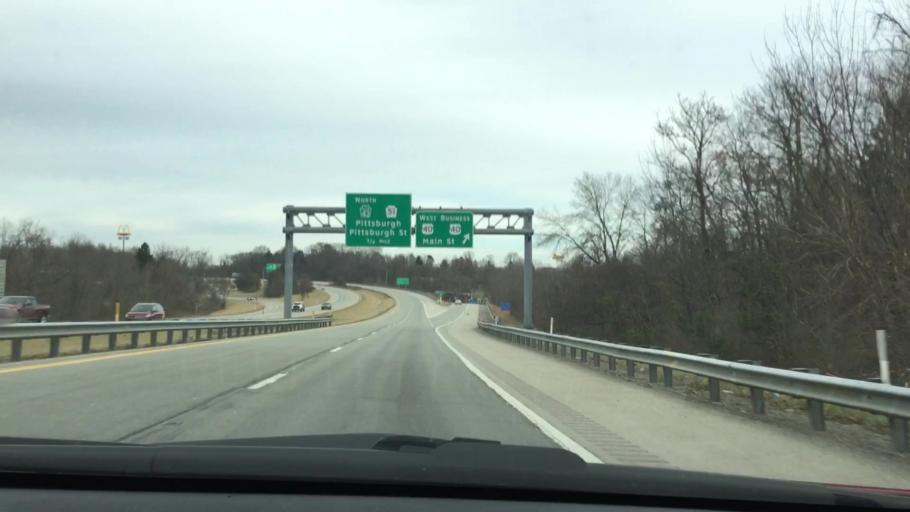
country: US
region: Pennsylvania
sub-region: Fayette County
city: South Uniontown
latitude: 39.9039
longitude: -79.7438
